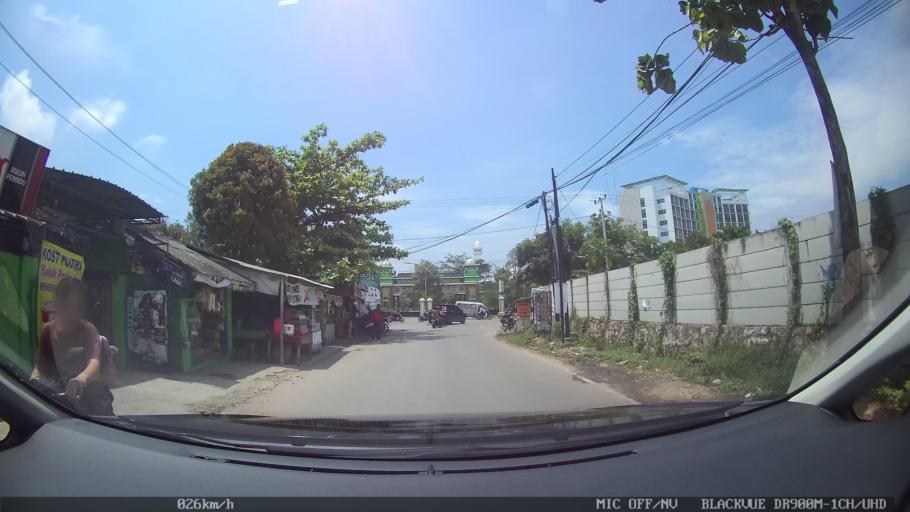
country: ID
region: Lampung
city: Kedaton
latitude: -5.3781
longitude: 105.3031
